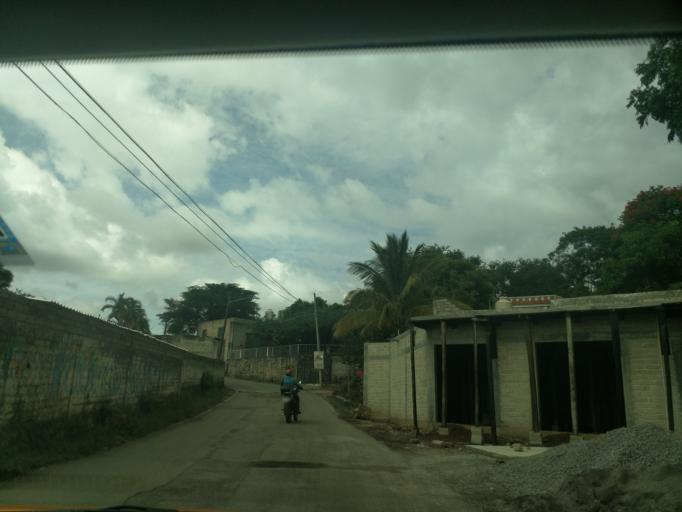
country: MX
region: Nayarit
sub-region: Tepic
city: La Corregidora
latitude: 21.4624
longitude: -104.7995
